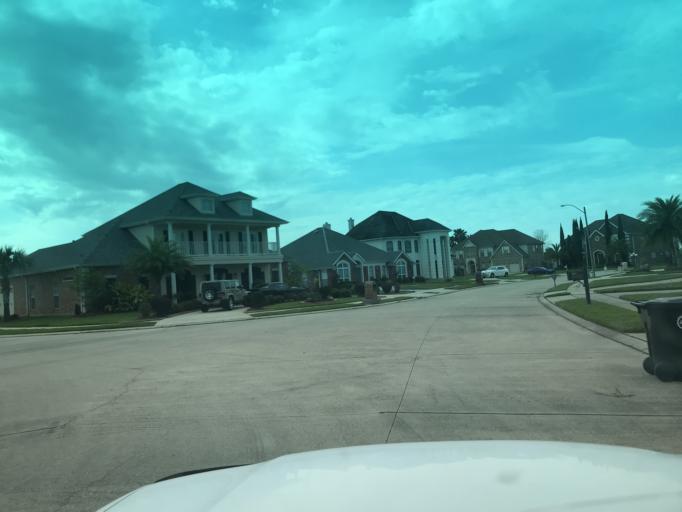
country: US
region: Louisiana
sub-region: Saint Bernard Parish
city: Chalmette
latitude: 30.0352
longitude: -89.9485
